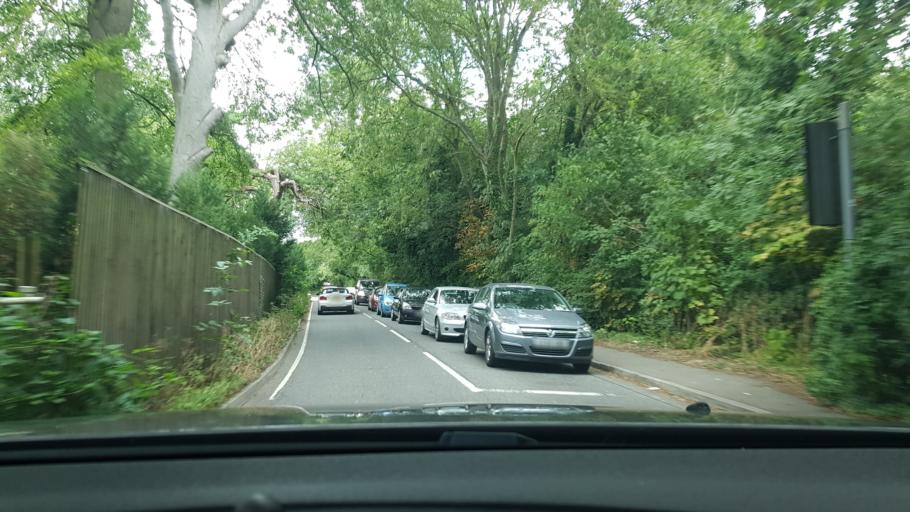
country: GB
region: England
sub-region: West Berkshire
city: Theale
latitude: 51.4298
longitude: -1.0711
